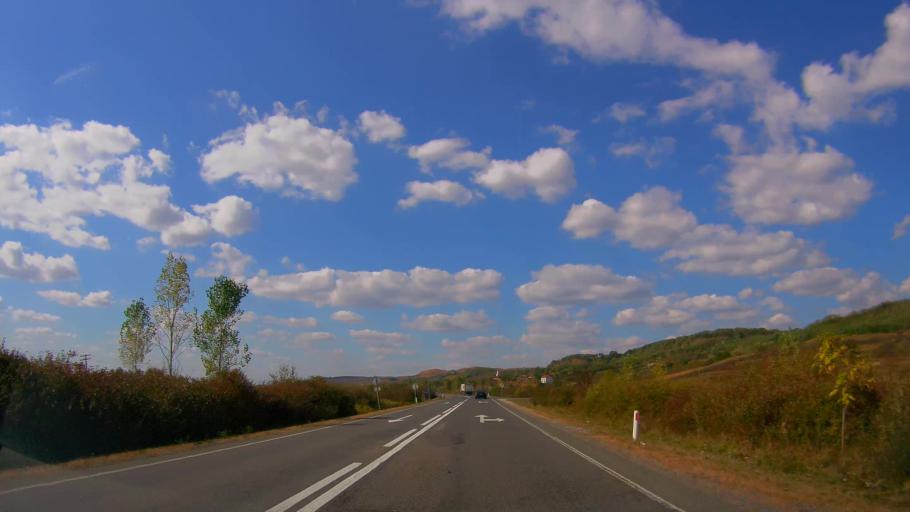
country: RO
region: Salaj
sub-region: Comuna Bocsa
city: Bocsa
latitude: 47.3127
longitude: 22.9139
